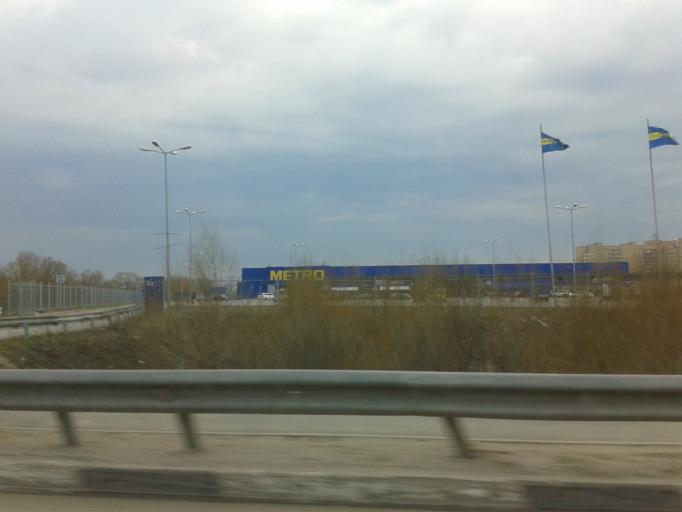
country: RU
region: Rjazan
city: Ryazan'
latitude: 54.6379
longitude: 39.6817
